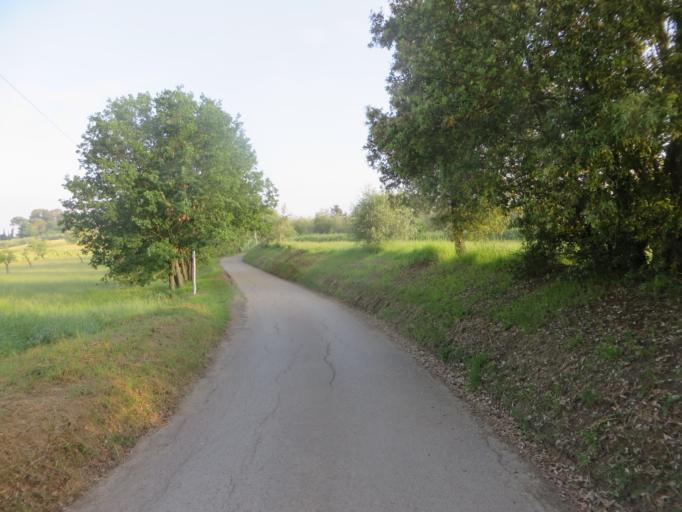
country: IT
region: Tuscany
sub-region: Province of Florence
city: Bagno a Ripoli
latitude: 43.7456
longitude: 11.3259
